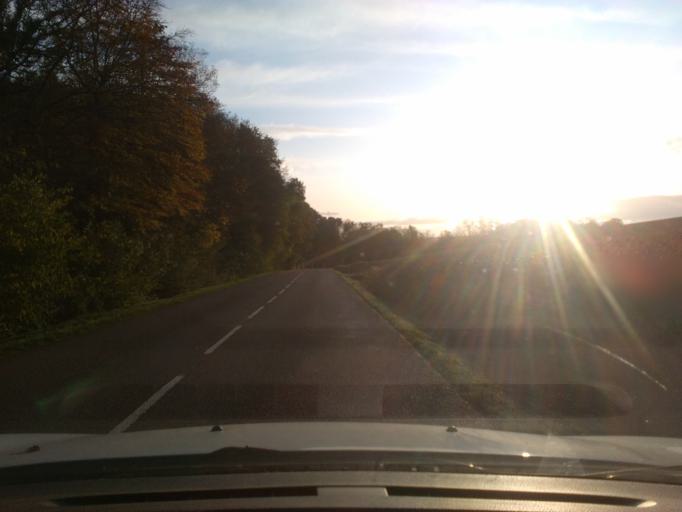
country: FR
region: Lorraine
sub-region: Departement des Vosges
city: Mirecourt
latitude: 48.2167
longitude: 6.1559
